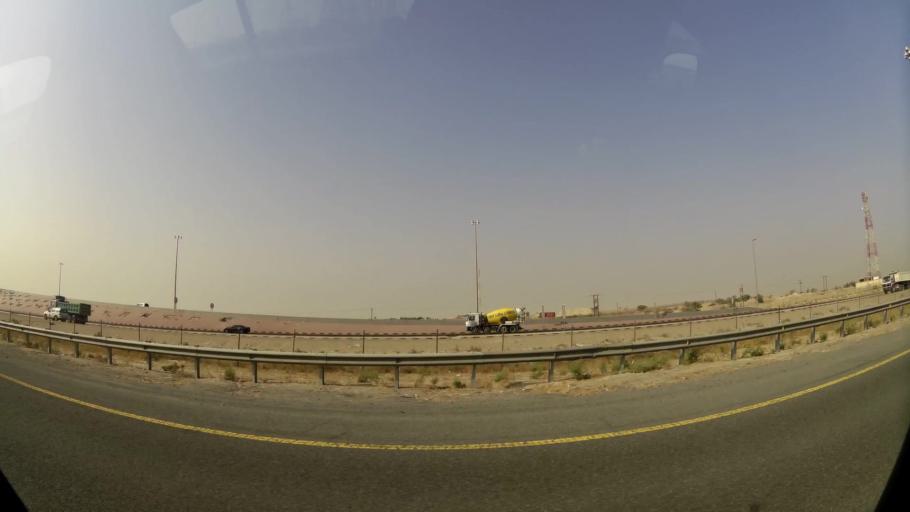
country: KW
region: Al Asimah
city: Ar Rabiyah
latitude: 29.2374
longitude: 47.8822
